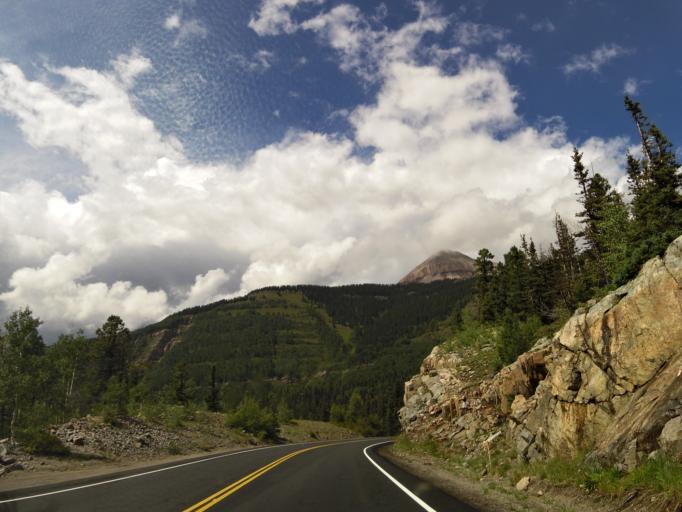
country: US
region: Colorado
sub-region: San Juan County
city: Silverton
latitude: 37.6778
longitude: -107.7832
